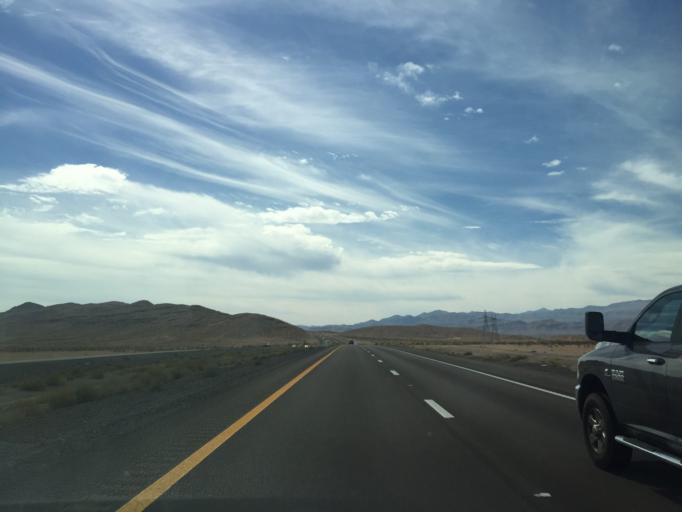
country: US
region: Nevada
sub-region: Clark County
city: Moapa Town
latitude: 36.4764
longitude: -114.8129
